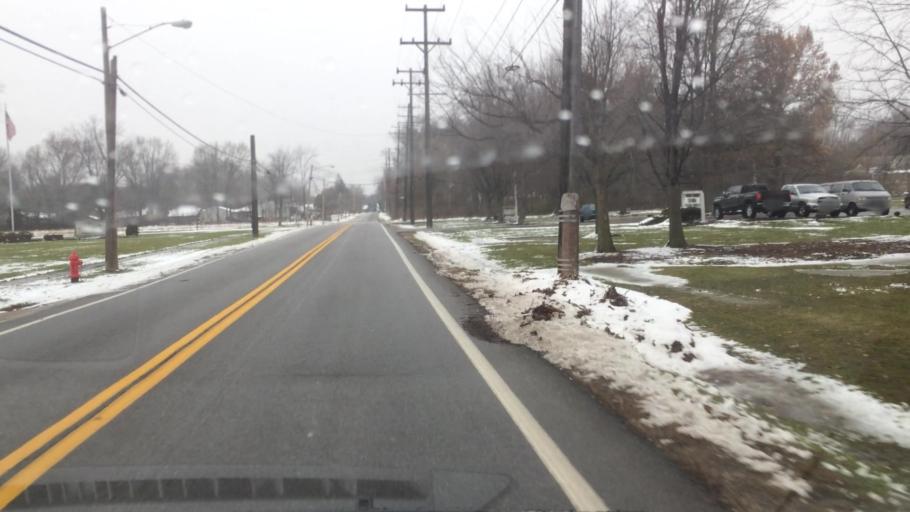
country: US
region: Ohio
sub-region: Cuyahoga County
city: Olmsted Falls
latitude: 41.3762
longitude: -81.9094
